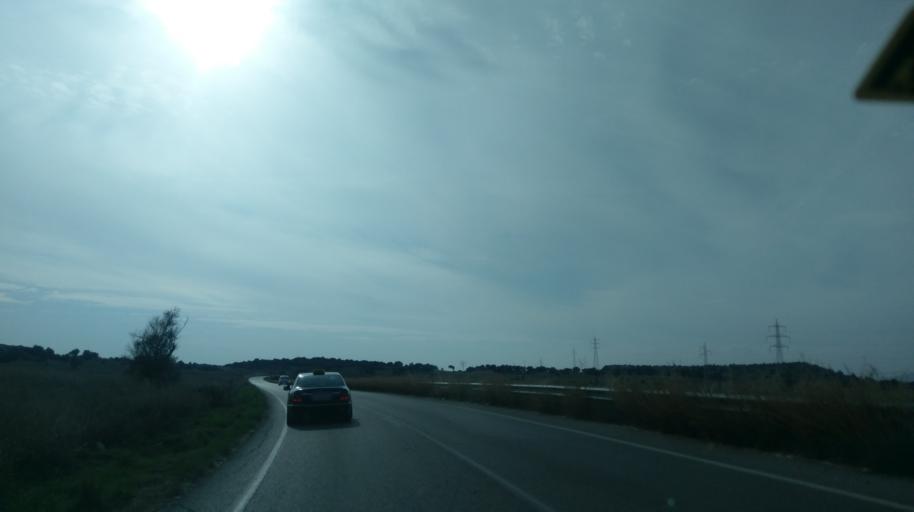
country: CY
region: Ammochostos
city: Leonarisso
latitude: 35.3941
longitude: 34.0613
